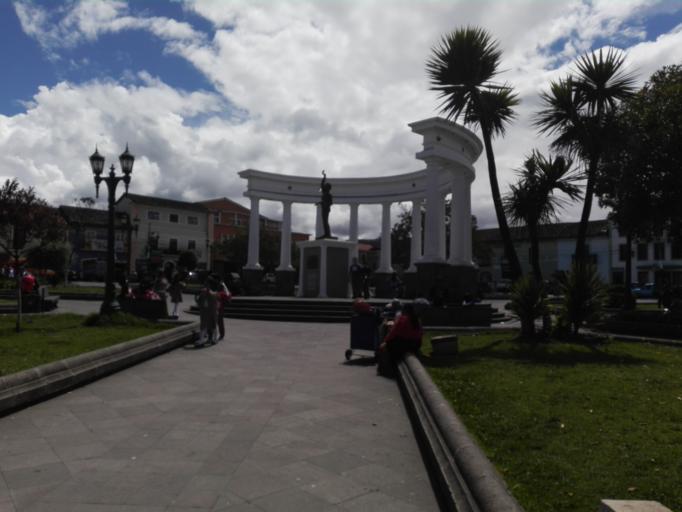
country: EC
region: Carchi
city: San Gabriel
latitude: 0.5982
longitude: -77.8353
